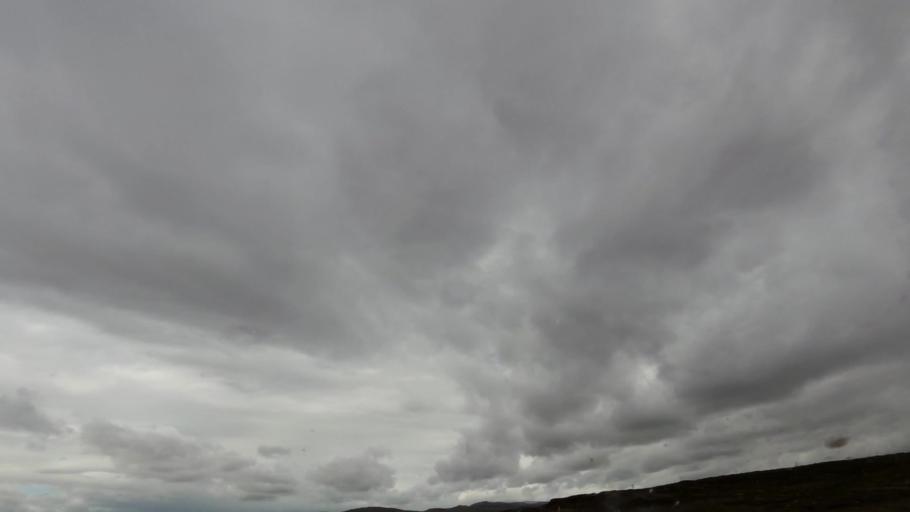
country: IS
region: West
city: Borgarnes
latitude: 65.1834
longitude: -21.7160
